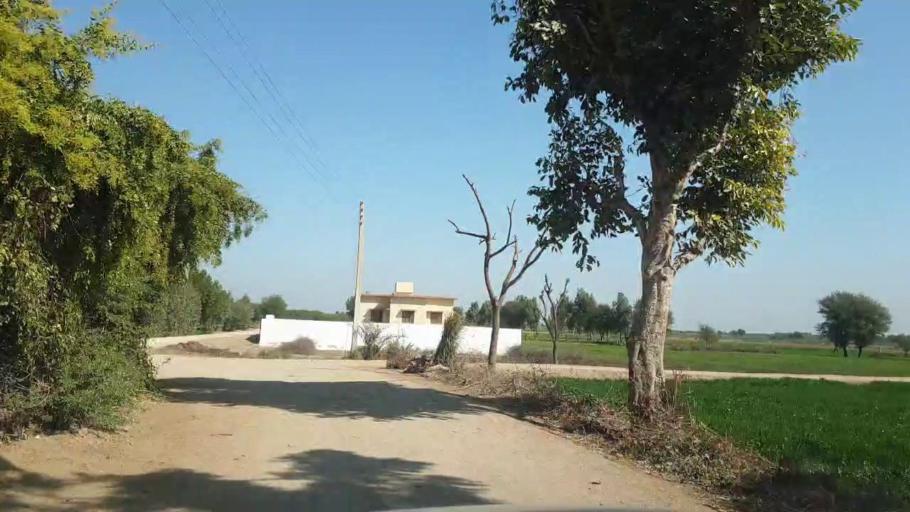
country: PK
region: Sindh
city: Tando Adam
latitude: 25.6497
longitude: 68.6987
